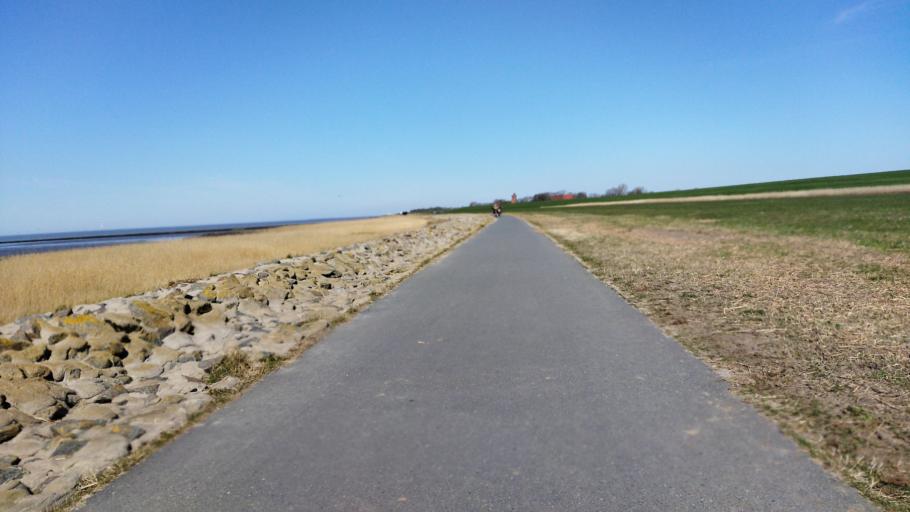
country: DE
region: Lower Saxony
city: Wremen
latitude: 53.6064
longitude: 8.5209
